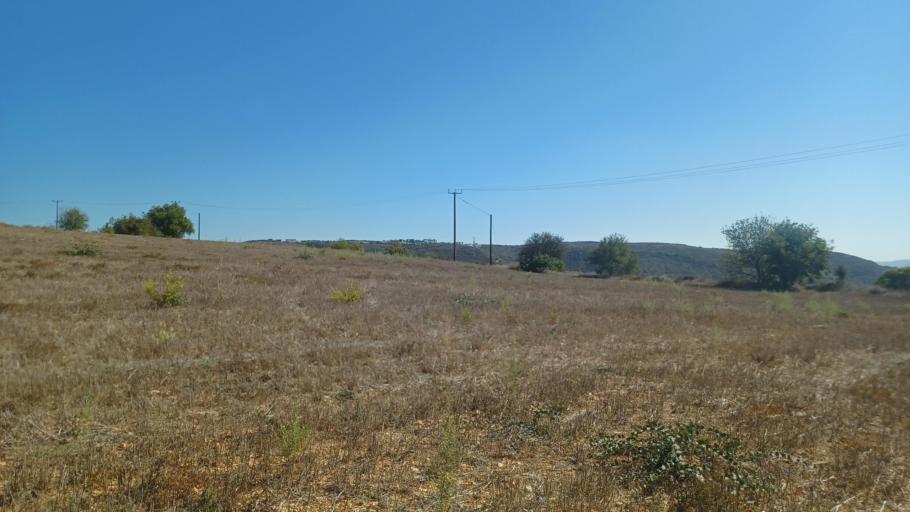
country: CY
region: Pafos
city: Mesogi
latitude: 34.8079
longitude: 32.4899
